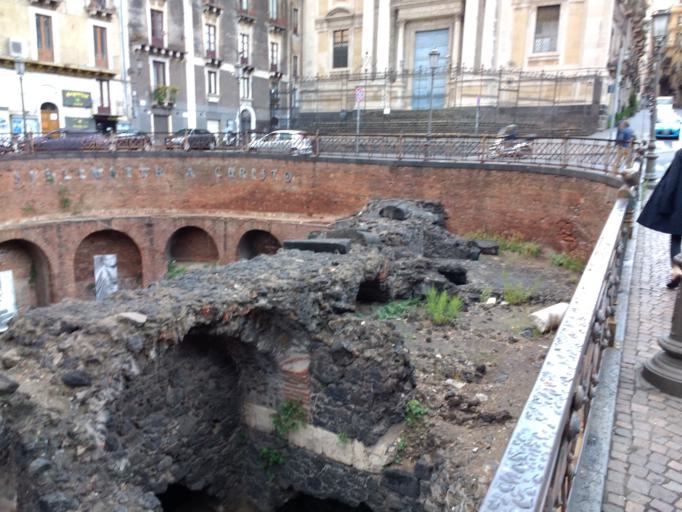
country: IT
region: Sicily
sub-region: Catania
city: Catania
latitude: 37.5075
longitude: 15.0853
